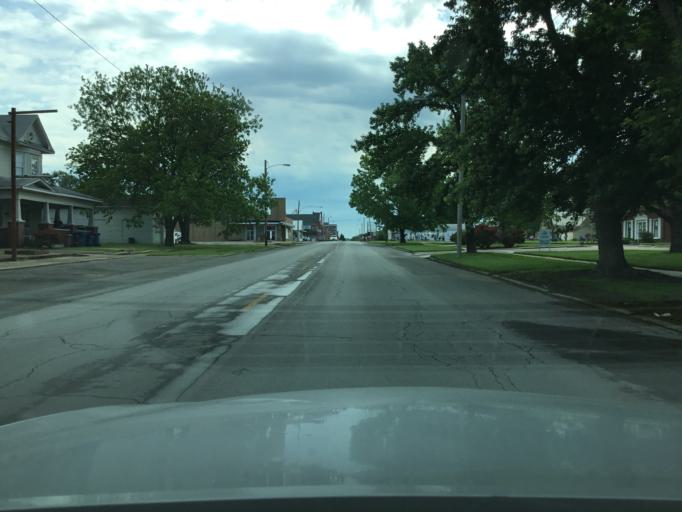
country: US
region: Kansas
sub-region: Montgomery County
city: Coffeyville
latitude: 37.0361
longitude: -95.6250
